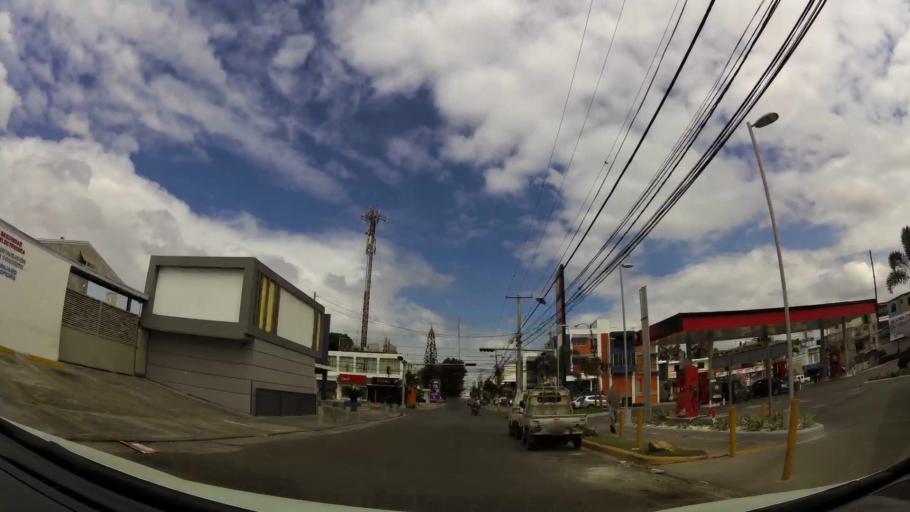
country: DO
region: Nacional
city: Bella Vista
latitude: 18.4760
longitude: -69.9541
